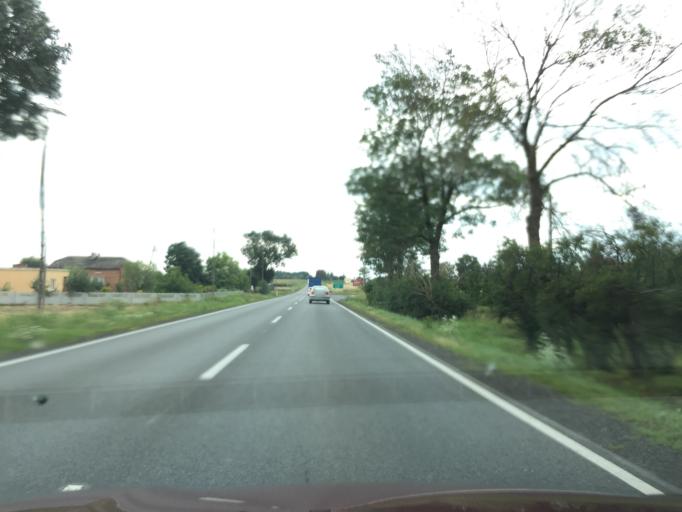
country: PL
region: Greater Poland Voivodeship
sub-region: Kalisz
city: Kalisz
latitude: 51.8256
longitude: 18.0942
